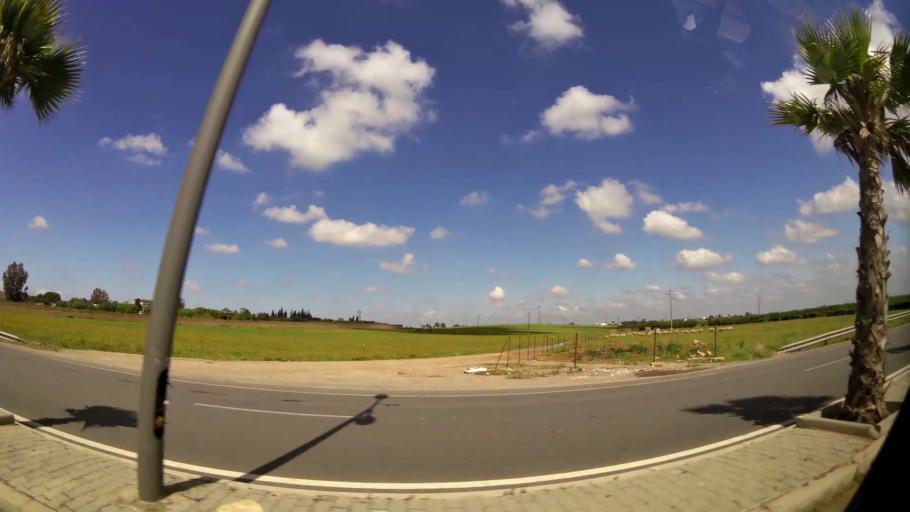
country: MA
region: Grand Casablanca
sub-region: Nouaceur
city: Bouskoura
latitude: 33.5044
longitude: -7.6098
